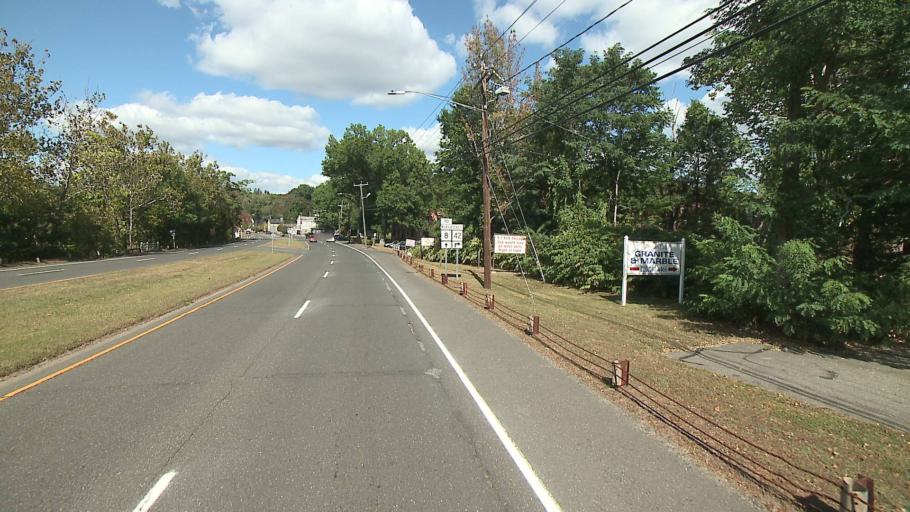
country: US
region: Connecticut
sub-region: New Haven County
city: Seymour
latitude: 41.4364
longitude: -73.0596
